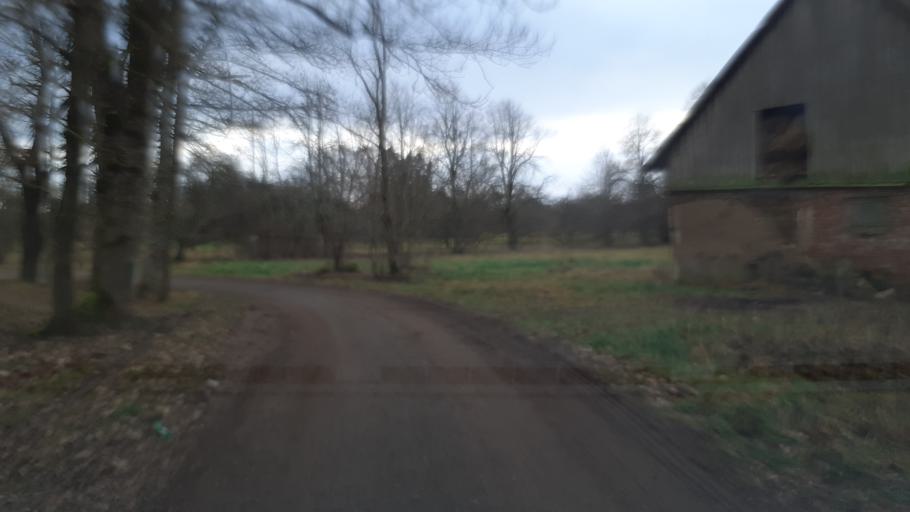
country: LV
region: Aizpute
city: Aizpute
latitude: 56.8013
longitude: 21.6671
